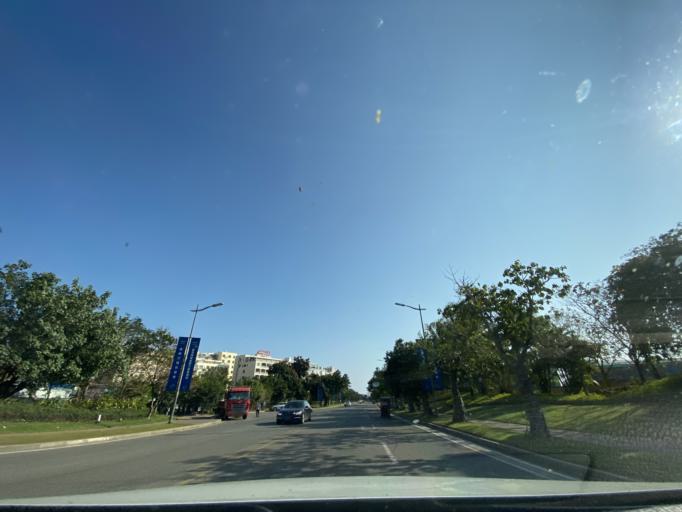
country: CN
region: Hainan
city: Xincun
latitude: 18.4191
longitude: 109.9611
